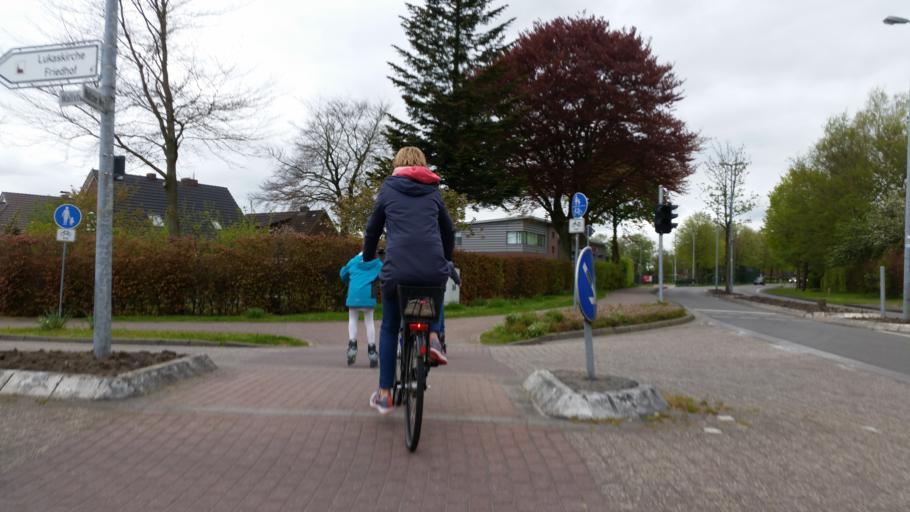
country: DE
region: Lower Saxony
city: Aurich
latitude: 53.4790
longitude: 7.4525
